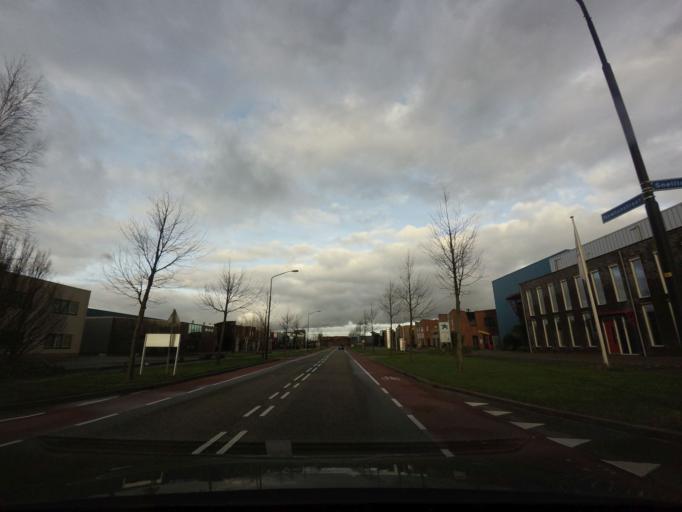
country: NL
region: North Holland
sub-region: Gemeente Heerhugowaard
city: Heerhugowaard
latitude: 52.6914
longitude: 4.8344
